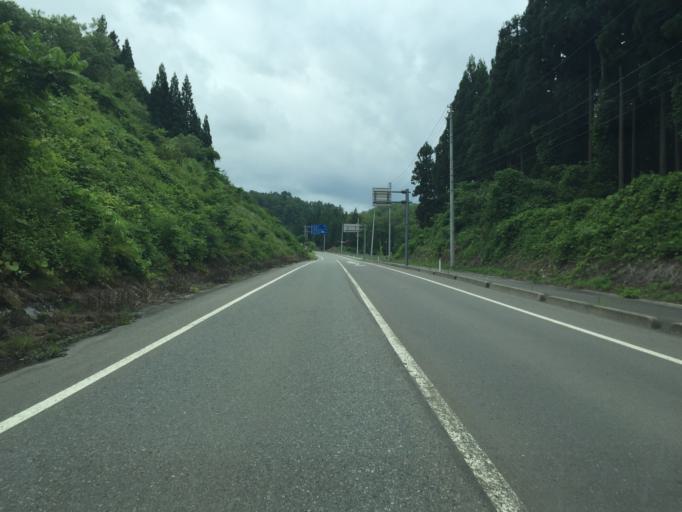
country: JP
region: Yamagata
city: Yonezawa
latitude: 37.8472
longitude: 140.0997
